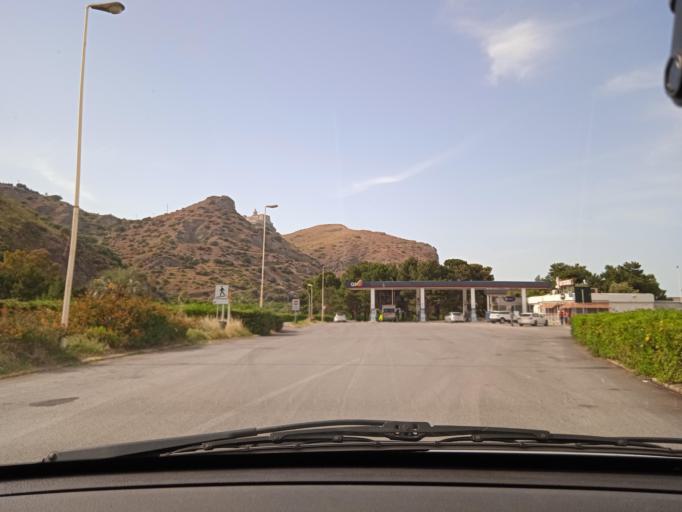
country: IT
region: Sicily
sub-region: Messina
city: Oliveri
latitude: 38.1273
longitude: 15.0538
